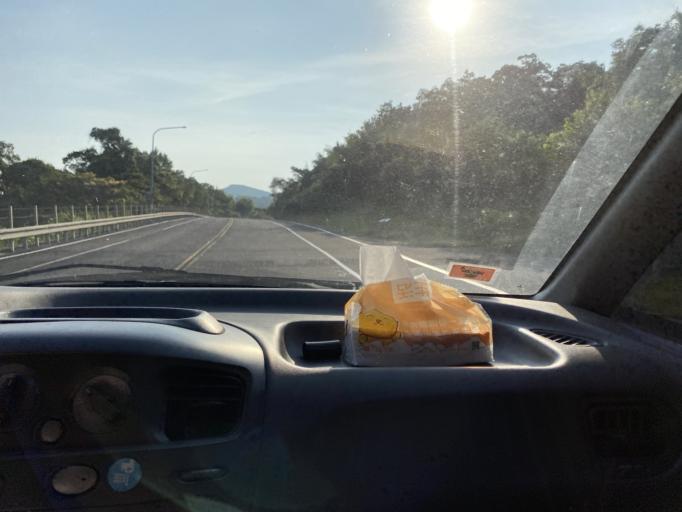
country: TW
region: Taiwan
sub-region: Keelung
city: Keelung
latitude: 25.0348
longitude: 121.8592
